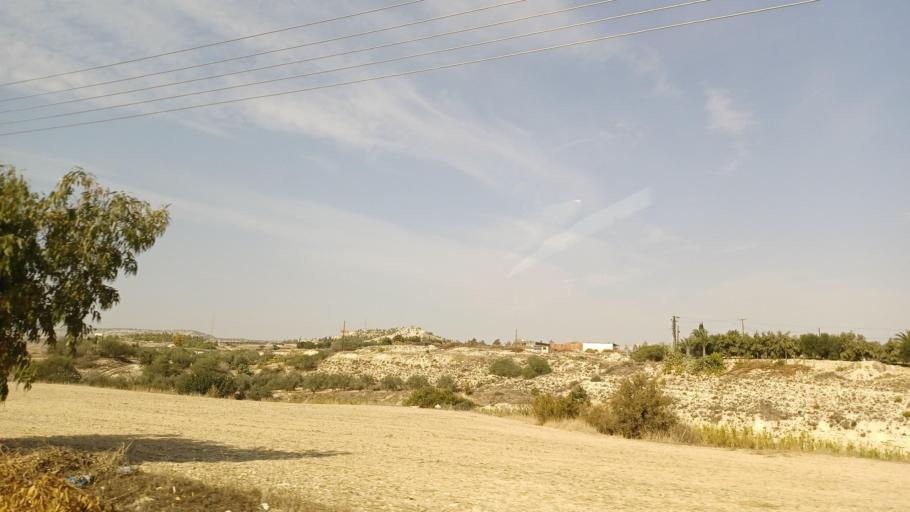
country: CY
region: Larnaka
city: Aradippou
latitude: 34.9640
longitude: 33.5536
